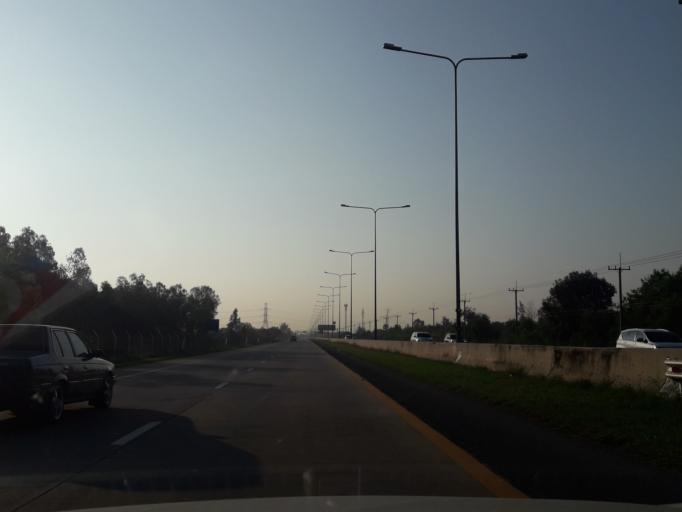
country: TH
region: Pathum Thani
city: Sam Khok
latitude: 14.1406
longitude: 100.5604
